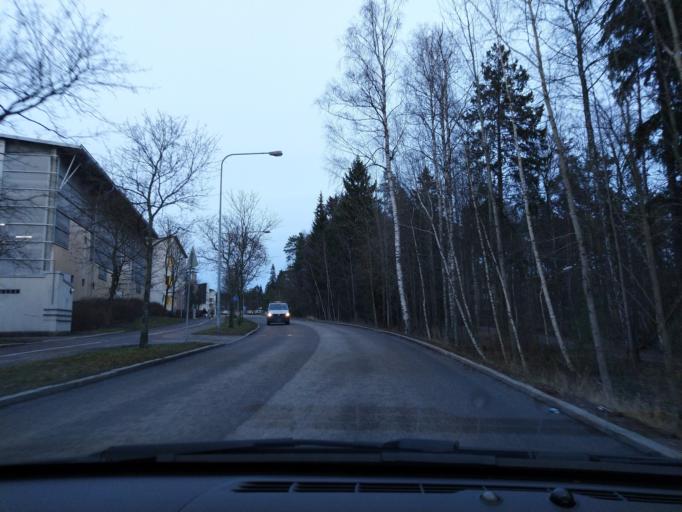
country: FI
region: Uusimaa
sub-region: Helsinki
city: Vantaa
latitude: 60.2353
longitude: 25.0655
